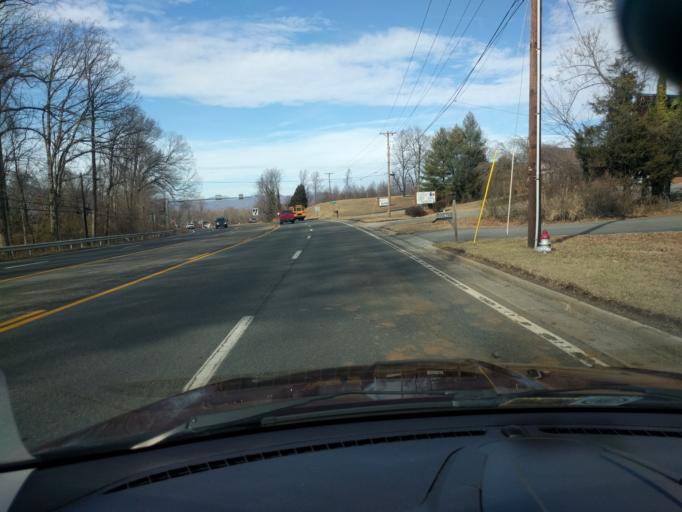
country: US
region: Virginia
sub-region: Amherst County
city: Madison Heights
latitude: 37.4918
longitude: -79.1244
